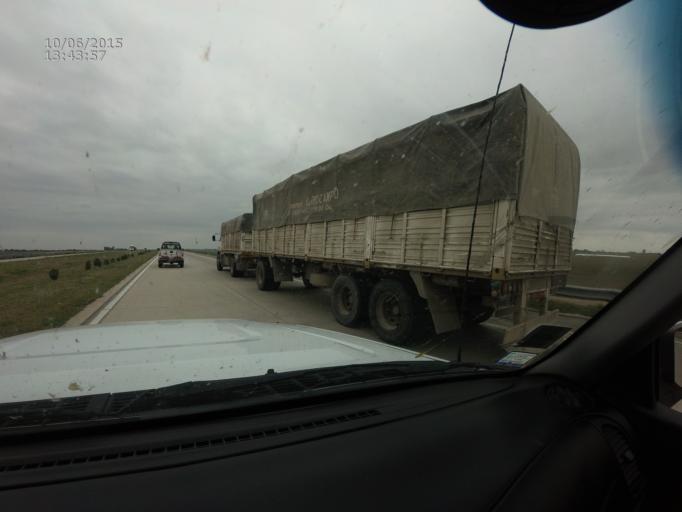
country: AR
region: Cordoba
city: Bell Ville
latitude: -32.5833
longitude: -62.5530
